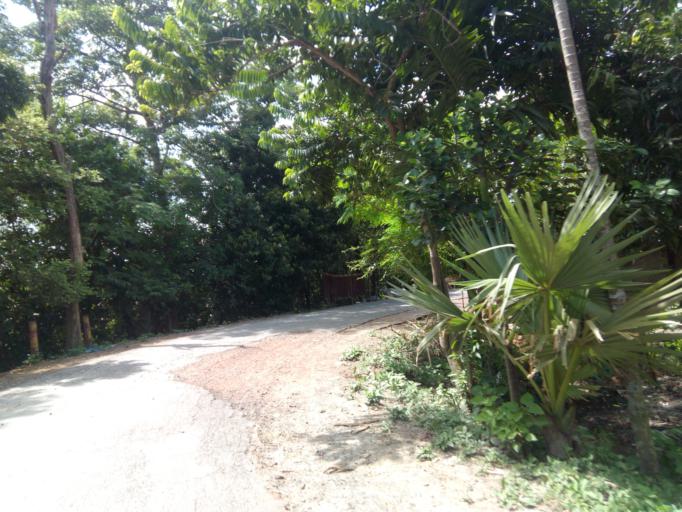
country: BD
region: Khulna
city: Kalia
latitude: 23.0145
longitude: 89.7193
